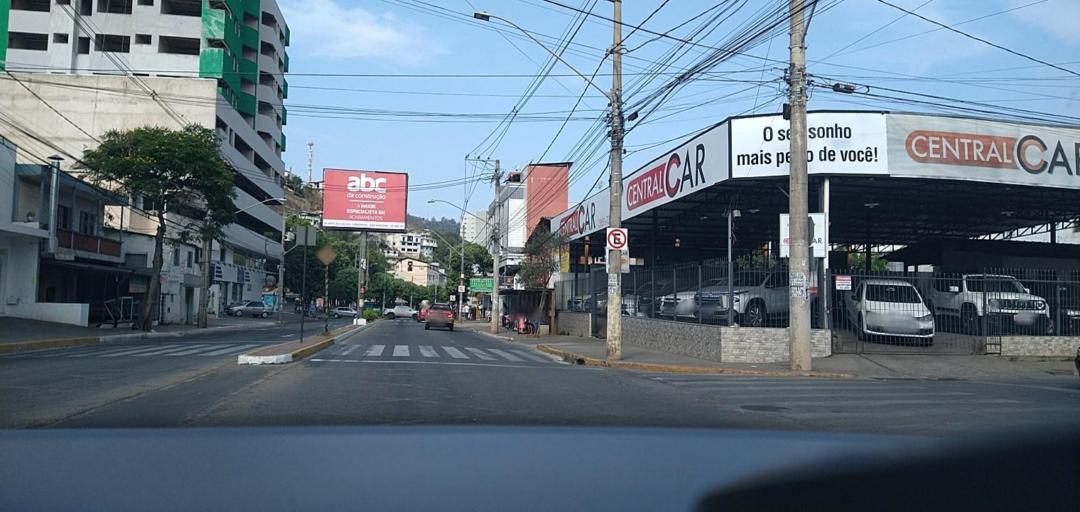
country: BR
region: Minas Gerais
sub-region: Joao Monlevade
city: Joao Monlevade
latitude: -19.8076
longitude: -43.1785
